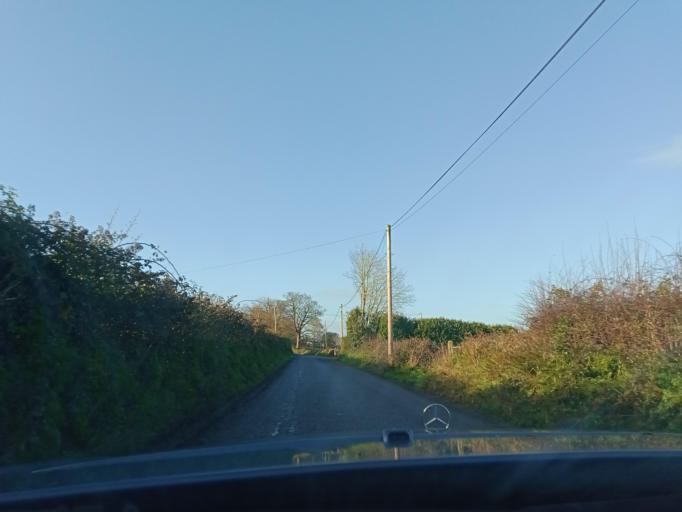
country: IE
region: Leinster
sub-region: Kilkenny
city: Callan
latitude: 52.4667
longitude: -7.4018
